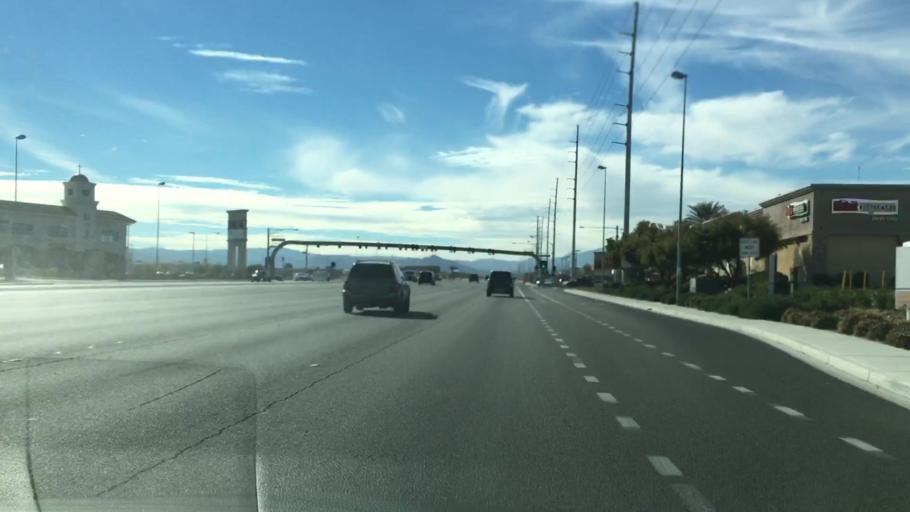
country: US
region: Nevada
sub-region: Clark County
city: Enterprise
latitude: 36.0335
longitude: -115.2064
